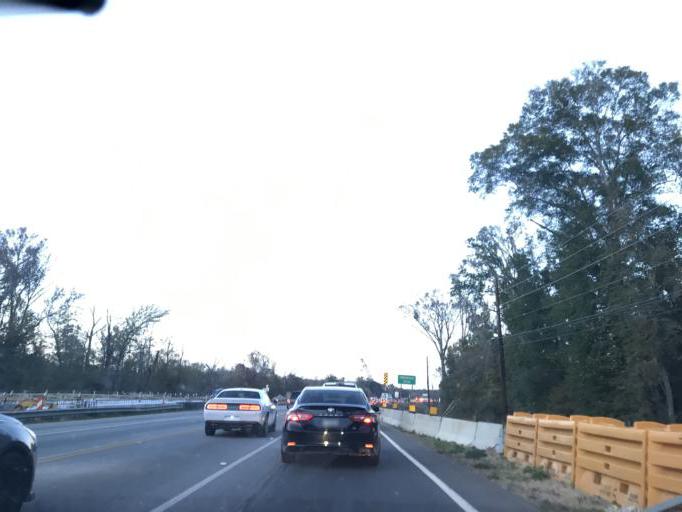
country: US
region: Georgia
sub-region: Bibb County
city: Macon
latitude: 32.7619
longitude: -83.6614
